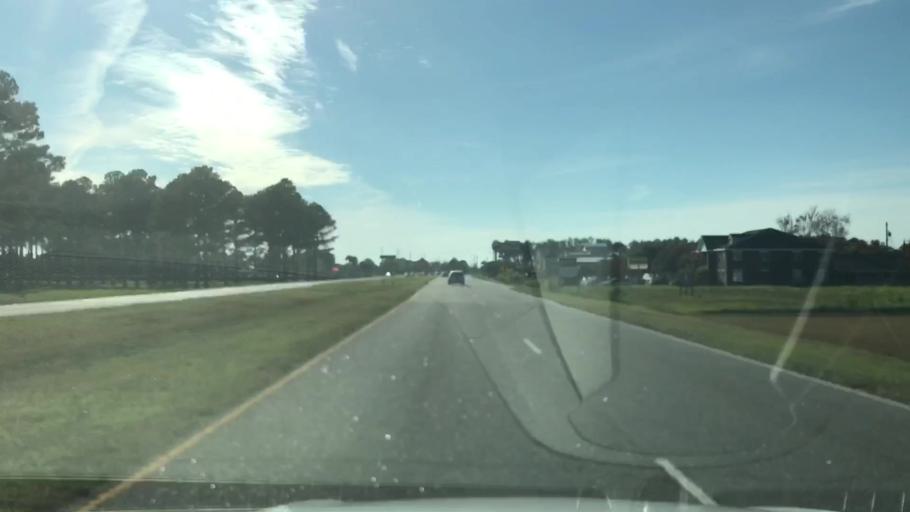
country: US
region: South Carolina
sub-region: Horry County
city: Myrtle Beach
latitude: 33.7233
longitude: -78.8772
